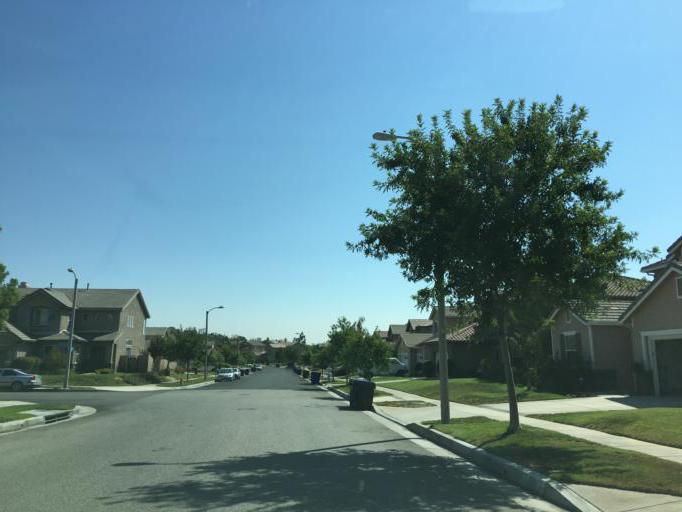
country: US
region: California
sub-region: Los Angeles County
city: Santa Clarita
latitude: 34.3858
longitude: -118.5754
